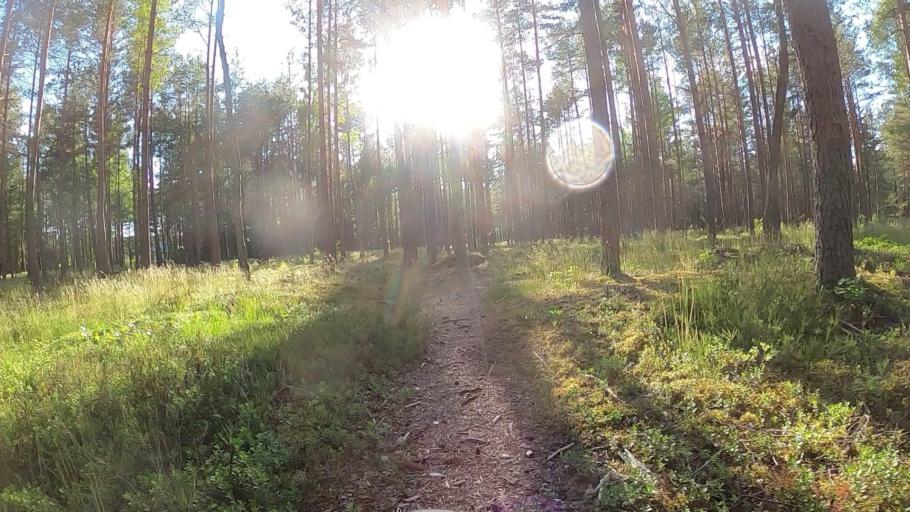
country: LV
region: Carnikava
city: Carnikava
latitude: 57.1344
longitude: 24.2554
